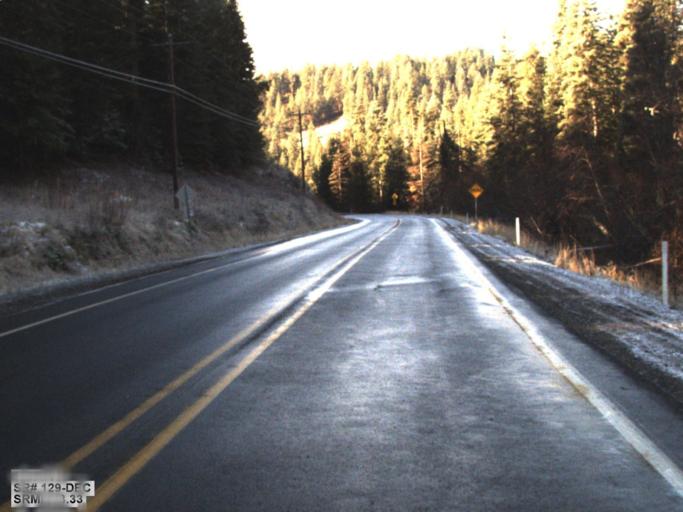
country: US
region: Washington
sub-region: Asotin County
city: Asotin
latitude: 46.0872
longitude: -117.1713
